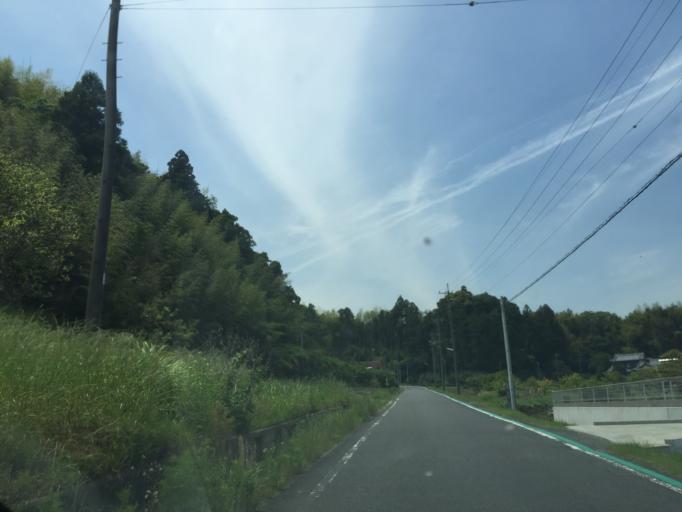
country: JP
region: Shizuoka
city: Kakegawa
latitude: 34.7950
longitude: 137.9711
